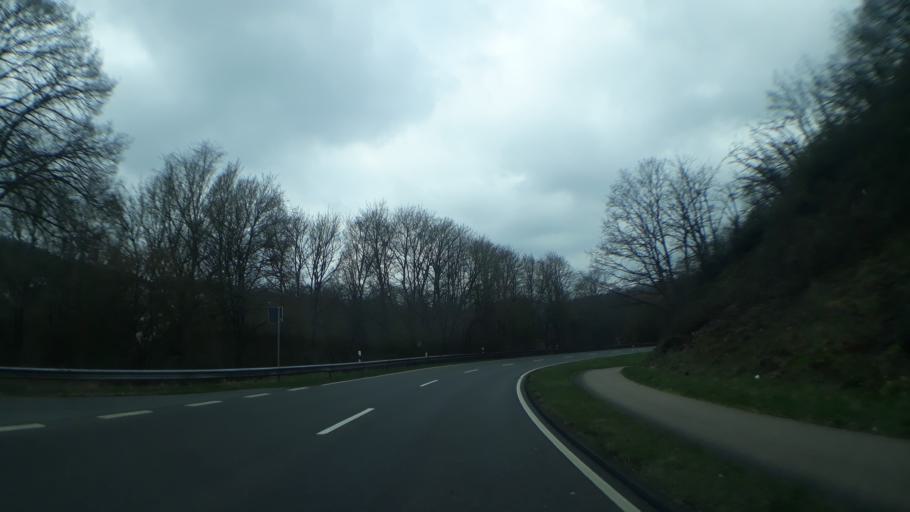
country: DE
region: North Rhine-Westphalia
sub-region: Regierungsbezirk Koln
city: Schleiden
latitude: 50.5358
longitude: 6.4869
